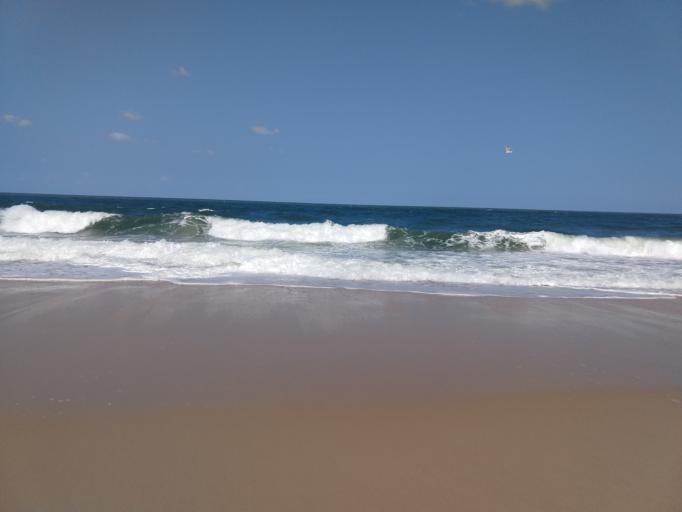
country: MZ
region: Sofala
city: Beira
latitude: -19.6579
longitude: 35.1706
